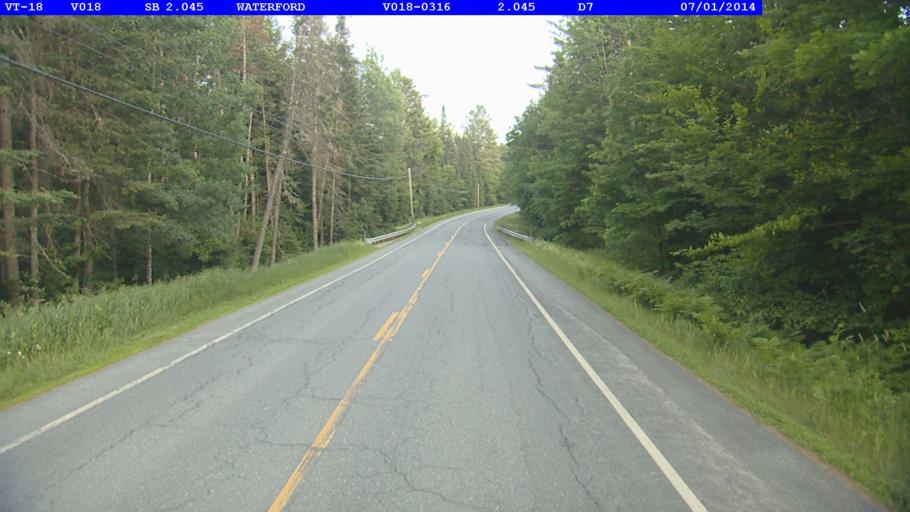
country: US
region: Vermont
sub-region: Caledonia County
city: Saint Johnsbury
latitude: 44.3662
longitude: -71.9055
